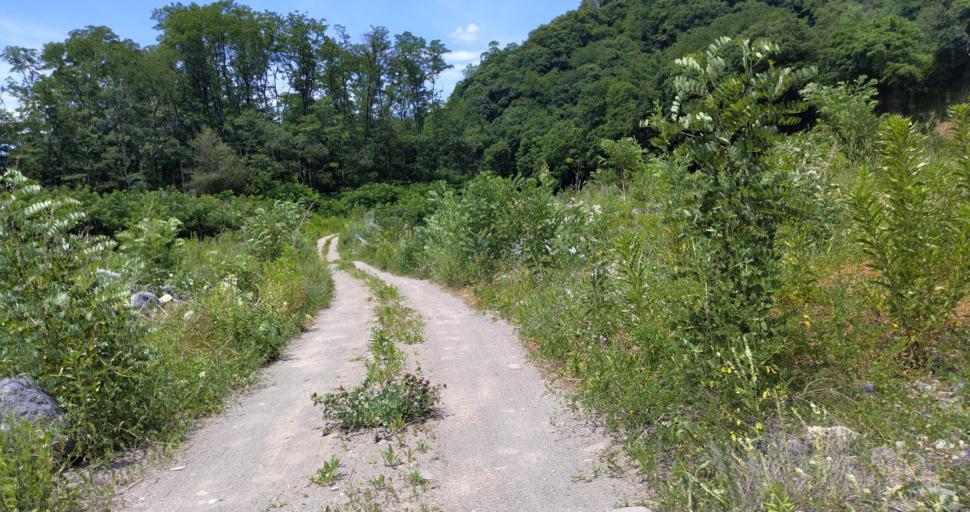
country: JP
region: Nagano
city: Komoro
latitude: 36.3248
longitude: 138.4145
